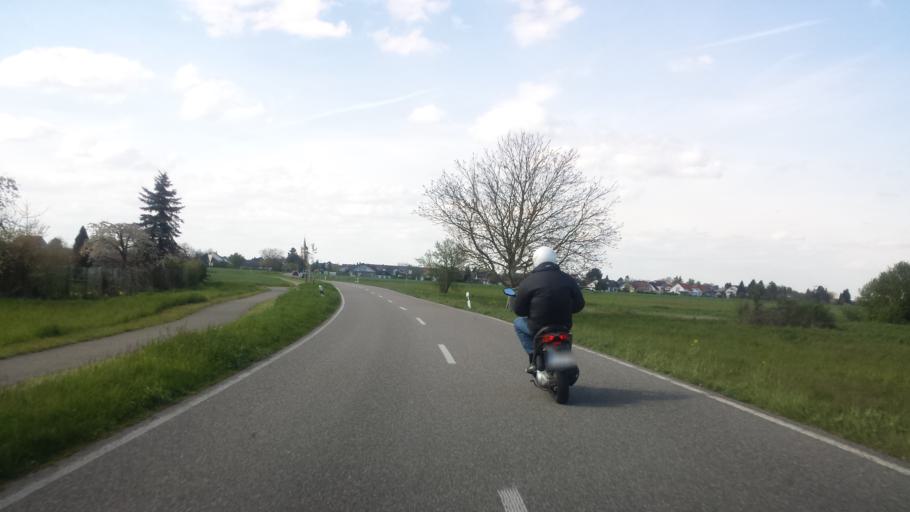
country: DE
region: Baden-Wuerttemberg
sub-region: Karlsruhe Region
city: Karlsdorf-Neuthard
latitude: 49.1173
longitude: 8.5260
